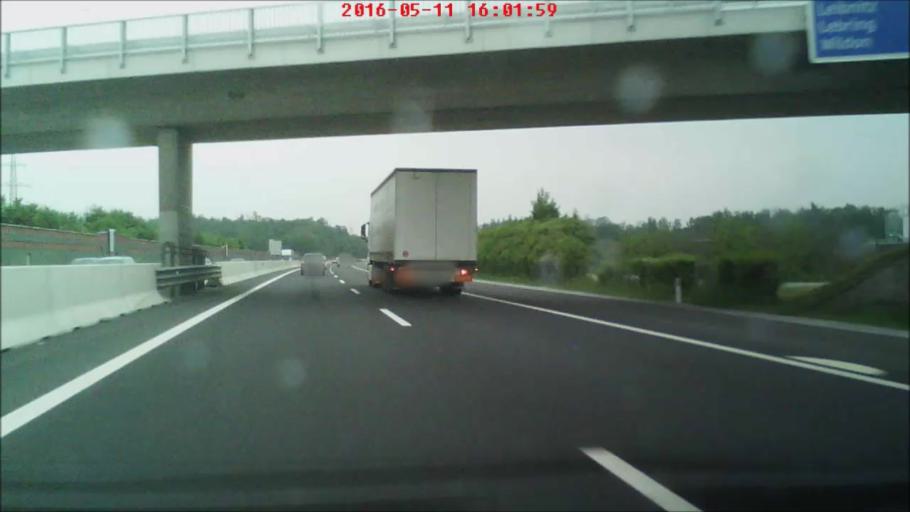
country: AT
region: Styria
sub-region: Politischer Bezirk Graz-Umgebung
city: Wundschuh
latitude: 46.9233
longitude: 15.4689
